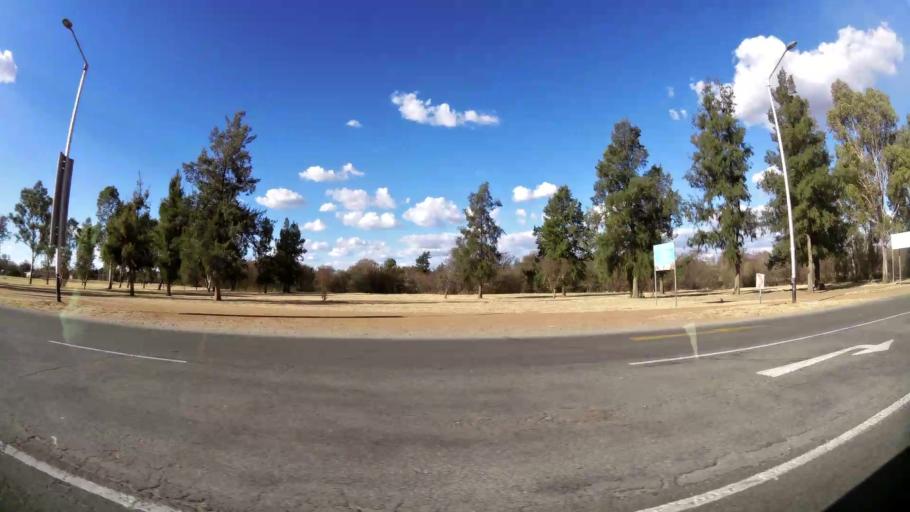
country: ZA
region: North-West
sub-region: Dr Kenneth Kaunda District Municipality
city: Klerksdorp
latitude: -26.8469
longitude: 26.6630
